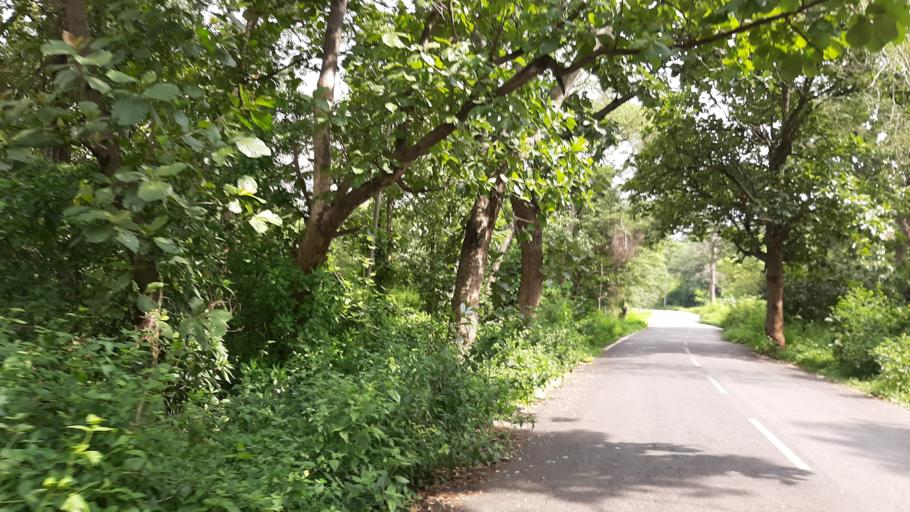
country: IN
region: Karnataka
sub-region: Ramanagara
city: Magadi
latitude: 12.9104
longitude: 77.2944
